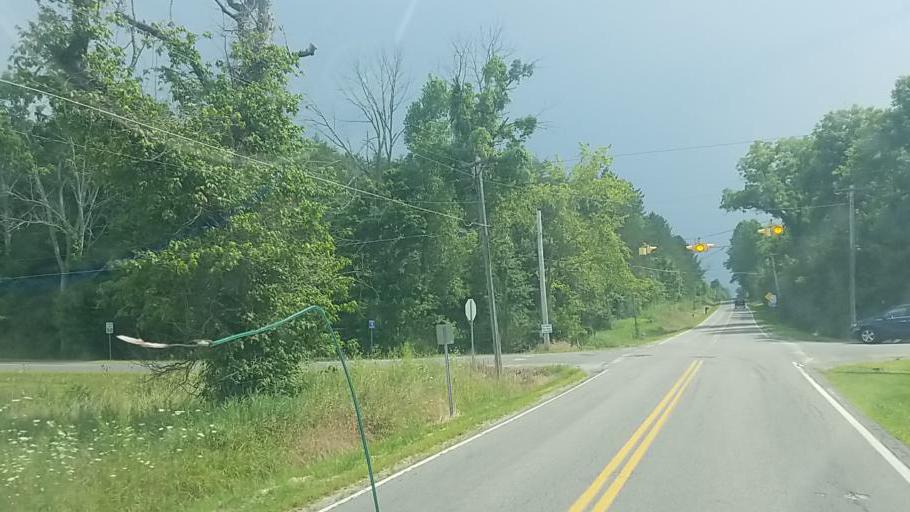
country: US
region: Ohio
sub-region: Medina County
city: Lodi
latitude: 41.0540
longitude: -82.0055
